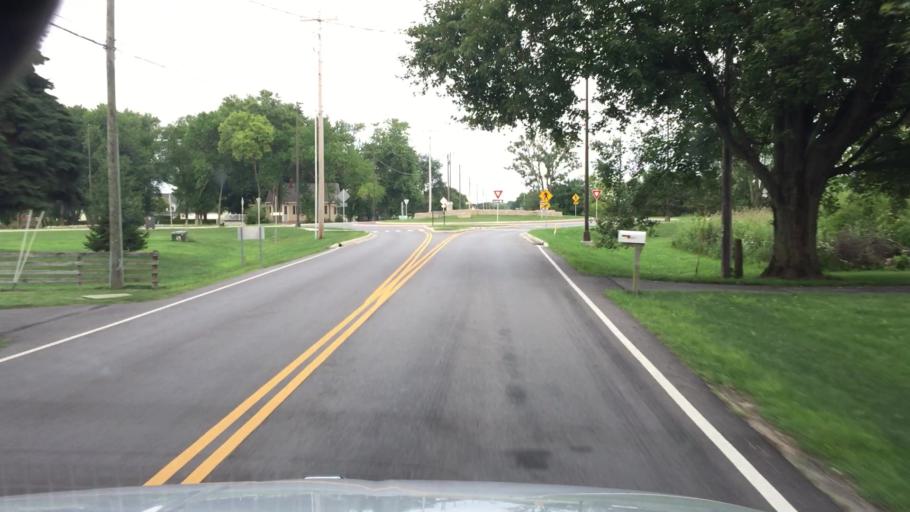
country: US
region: Ohio
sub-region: Franklin County
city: Hilliard
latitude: 40.0771
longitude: -83.1764
